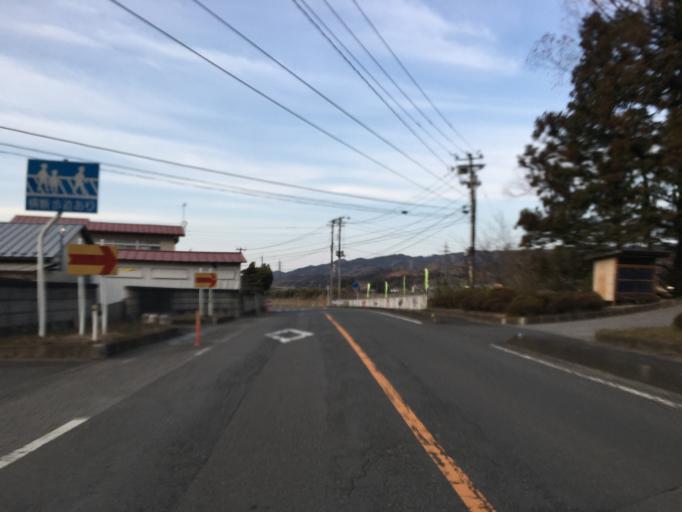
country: JP
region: Ibaraki
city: Daigo
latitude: 36.8768
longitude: 140.4150
